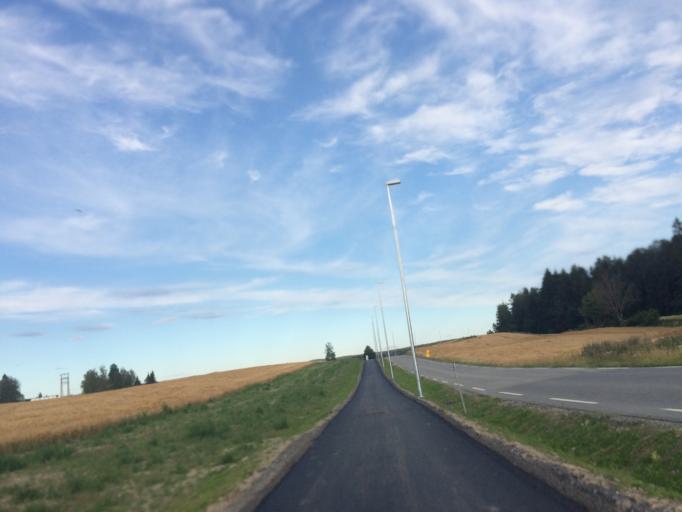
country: NO
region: Akershus
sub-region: Ski
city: Ski
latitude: 59.6967
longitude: 10.8534
